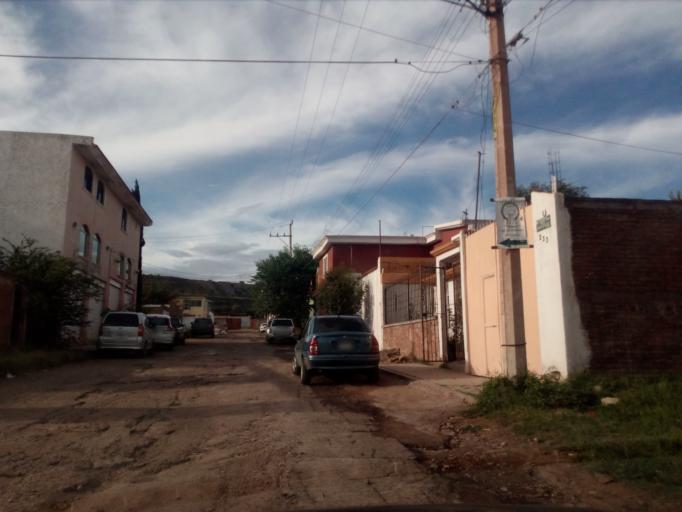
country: MX
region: Durango
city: Victoria de Durango
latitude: 24.0491
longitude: -104.6620
